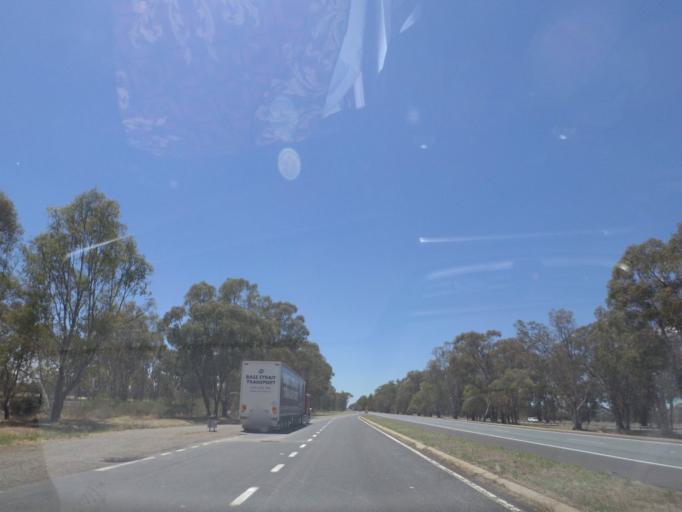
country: AU
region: Victoria
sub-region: Benalla
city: Benalla
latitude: -36.6191
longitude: 145.7741
